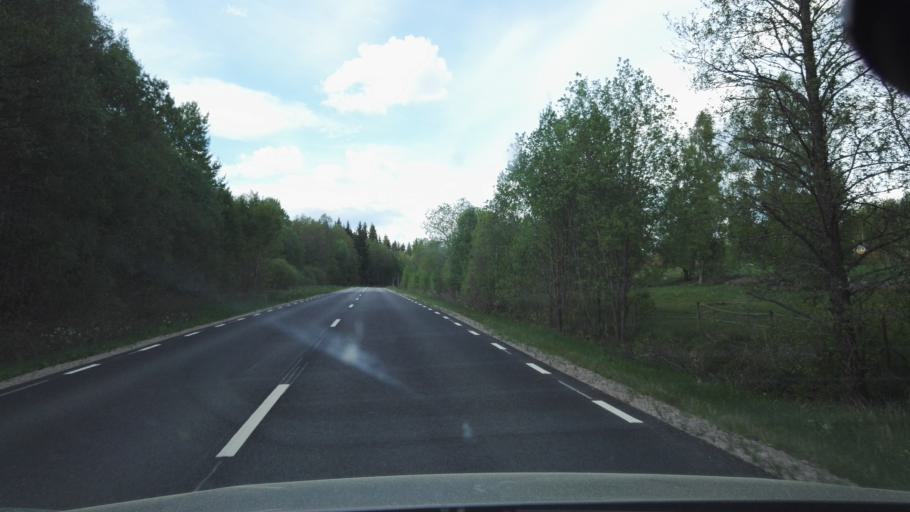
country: SE
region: Kronoberg
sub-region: Vaxjo Kommun
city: Braas
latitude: 57.1636
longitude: 14.9607
